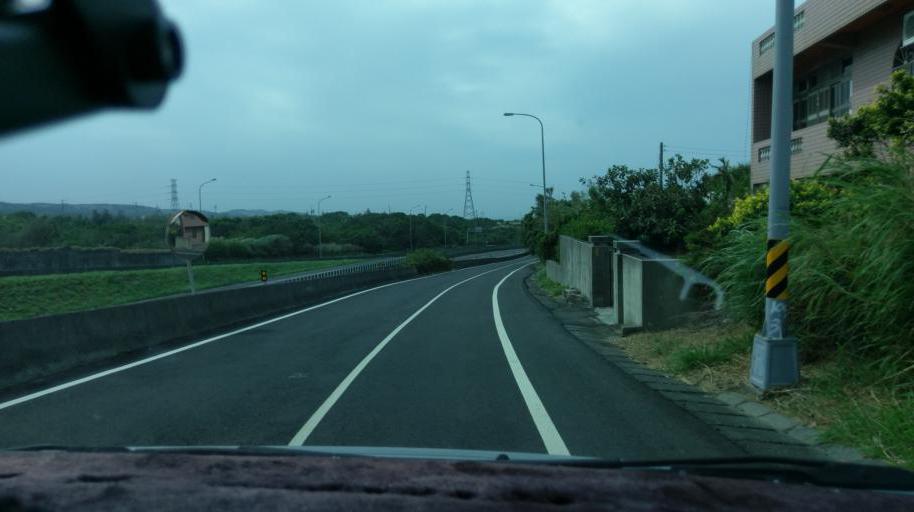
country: TW
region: Taiwan
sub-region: Miaoli
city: Miaoli
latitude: 24.5876
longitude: 120.7304
